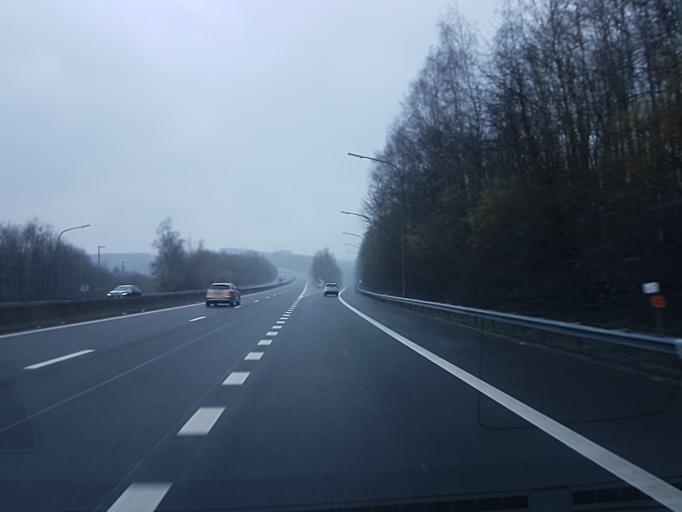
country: BE
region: Wallonia
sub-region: Province de Liege
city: Malmedy
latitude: 50.4189
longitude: 5.9972
